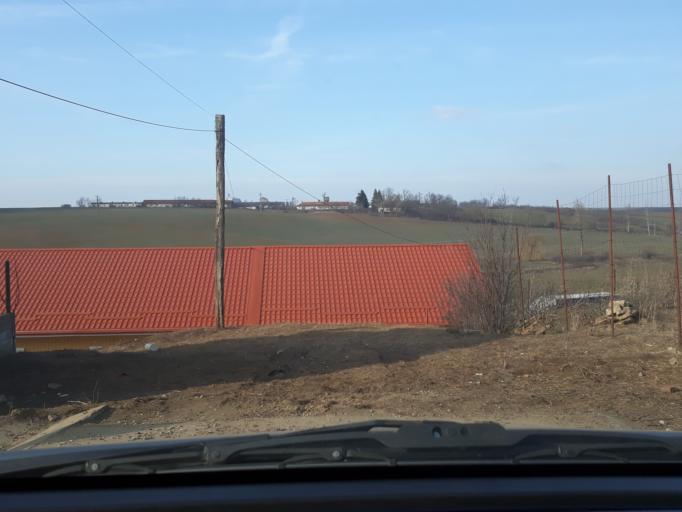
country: RO
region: Bihor
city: Margita
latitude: 47.3614
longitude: 22.3298
